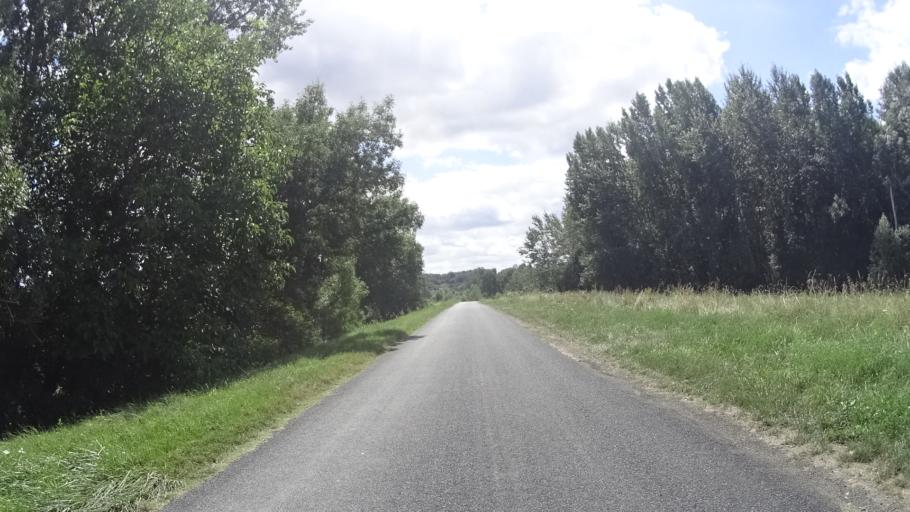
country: FR
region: Centre
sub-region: Departement d'Indre-et-Loire
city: Cinq-Mars-la-Pile
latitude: 47.3397
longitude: 0.4834
